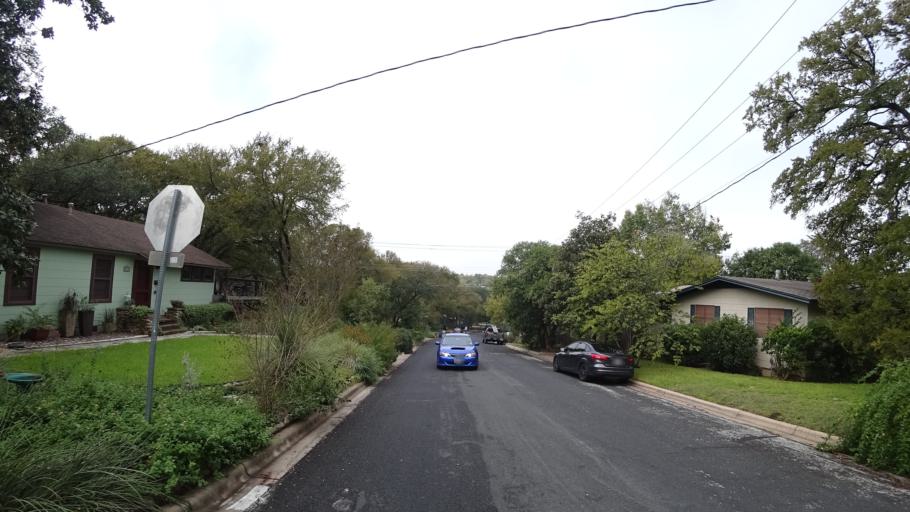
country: US
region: Texas
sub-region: Travis County
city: Rollingwood
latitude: 30.2483
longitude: -97.7814
